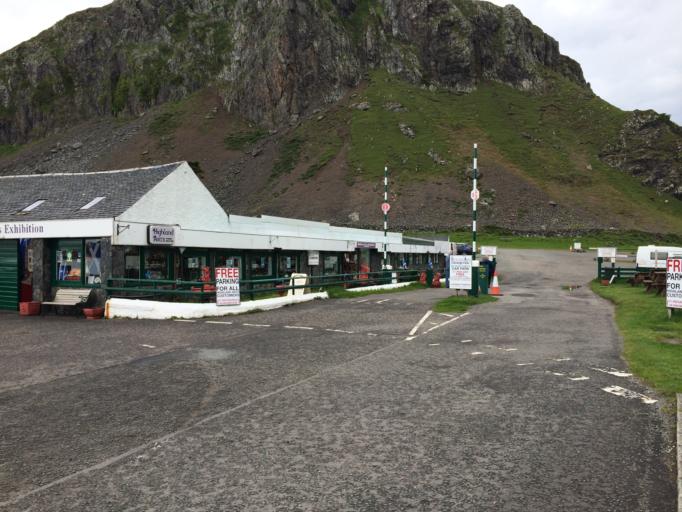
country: GB
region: Scotland
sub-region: Argyll and Bute
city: Isle Of Mull
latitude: 56.2948
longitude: -5.6494
